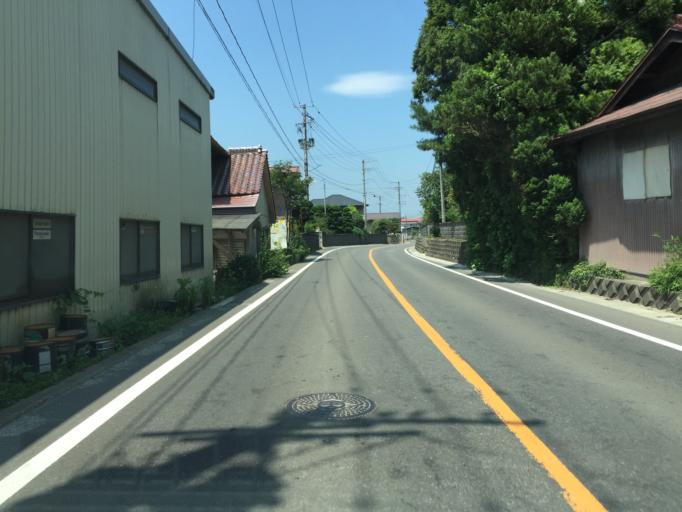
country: JP
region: Miyagi
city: Marumori
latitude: 37.8952
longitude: 140.8010
